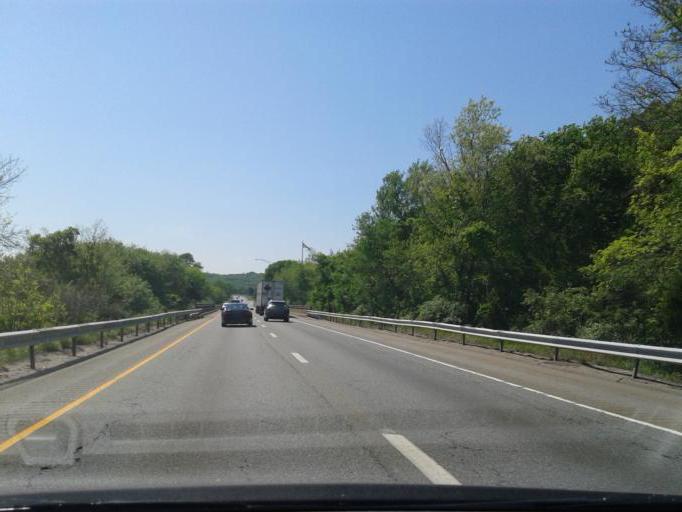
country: US
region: Connecticut
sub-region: New London County
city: Old Mystic
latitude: 41.3742
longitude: -71.9473
